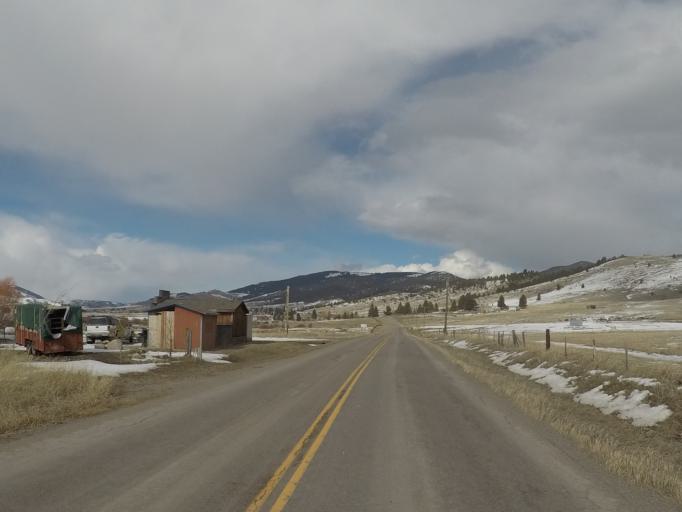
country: US
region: Montana
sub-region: Granite County
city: Philipsburg
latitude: 46.3105
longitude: -113.3041
